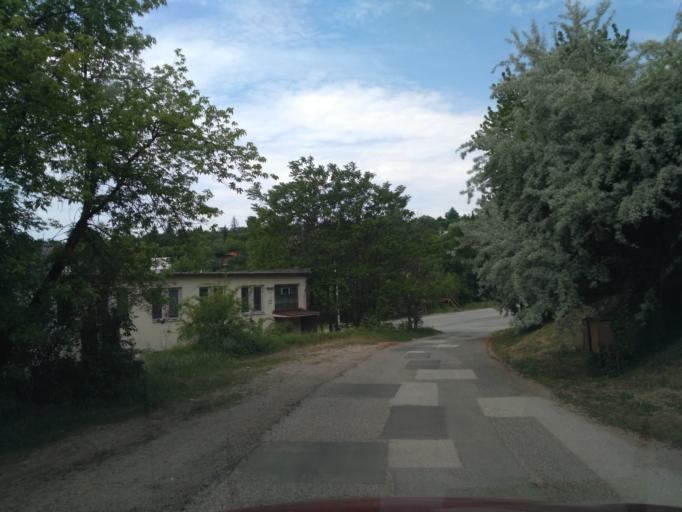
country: SK
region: Kosicky
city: Kosice
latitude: 48.7327
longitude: 21.2288
